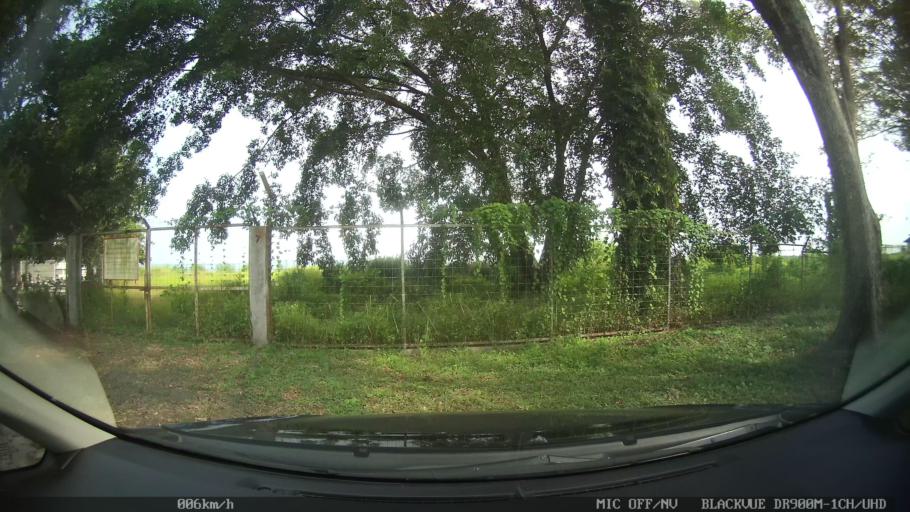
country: ID
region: Daerah Istimewa Yogyakarta
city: Depok
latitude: -7.7849
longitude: 110.4419
